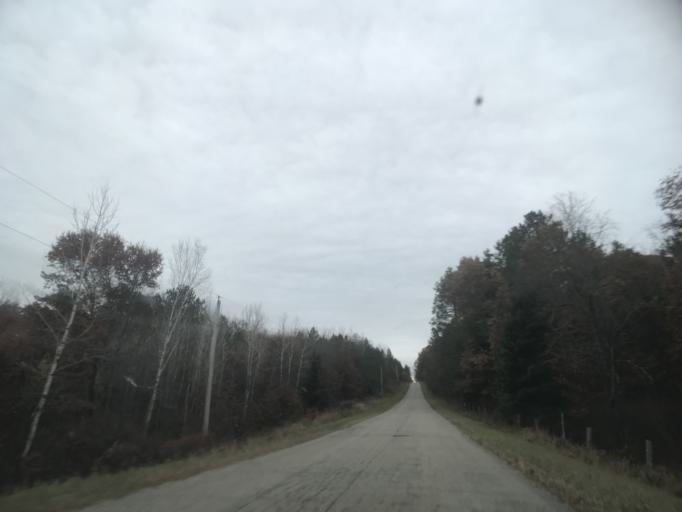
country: US
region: Wisconsin
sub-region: Oconto County
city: Gillett
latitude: 45.3270
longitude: -88.2761
